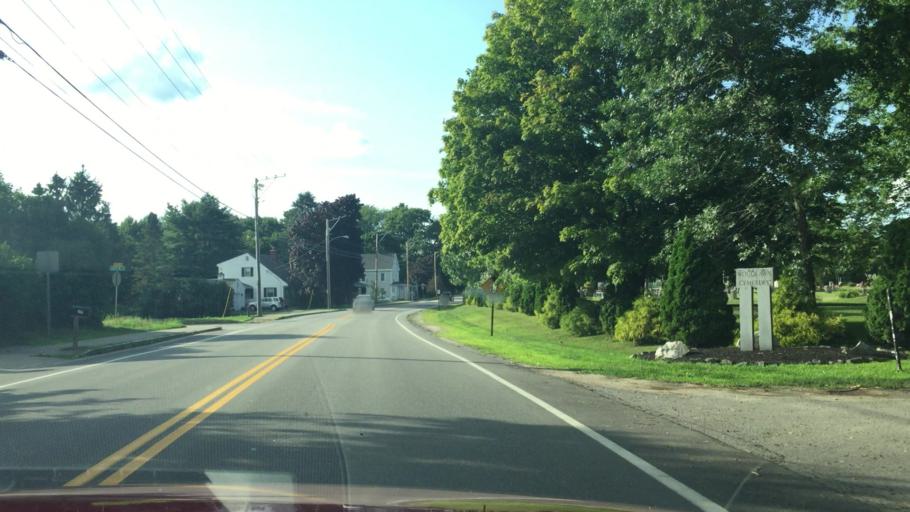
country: US
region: Maine
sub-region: Cumberland County
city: Westbrook
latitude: 43.6665
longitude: -70.3473
